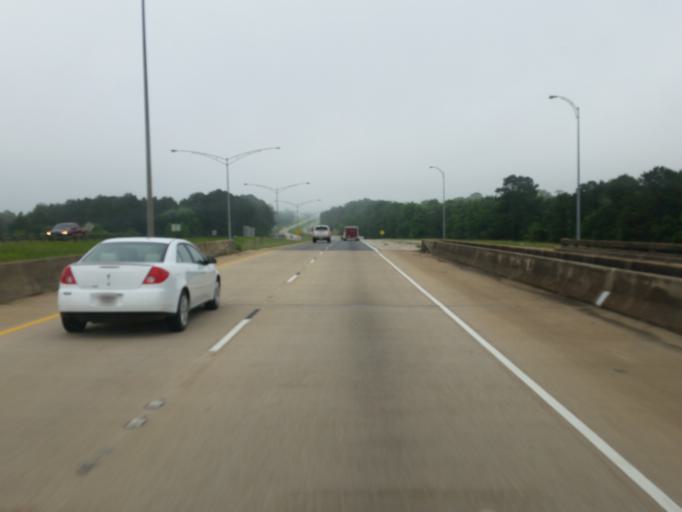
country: US
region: Louisiana
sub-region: Webster Parish
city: Minden
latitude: 32.5891
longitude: -93.2916
